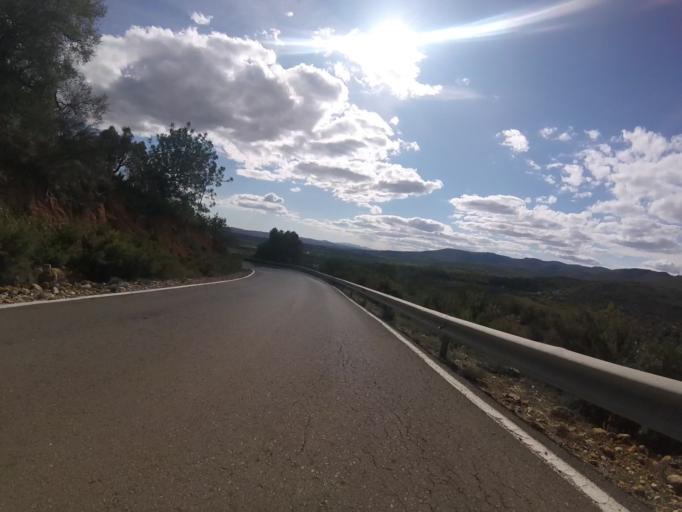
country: ES
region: Valencia
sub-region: Provincia de Castello
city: Cuevas de Vinroma
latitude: 40.3761
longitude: 0.1131
